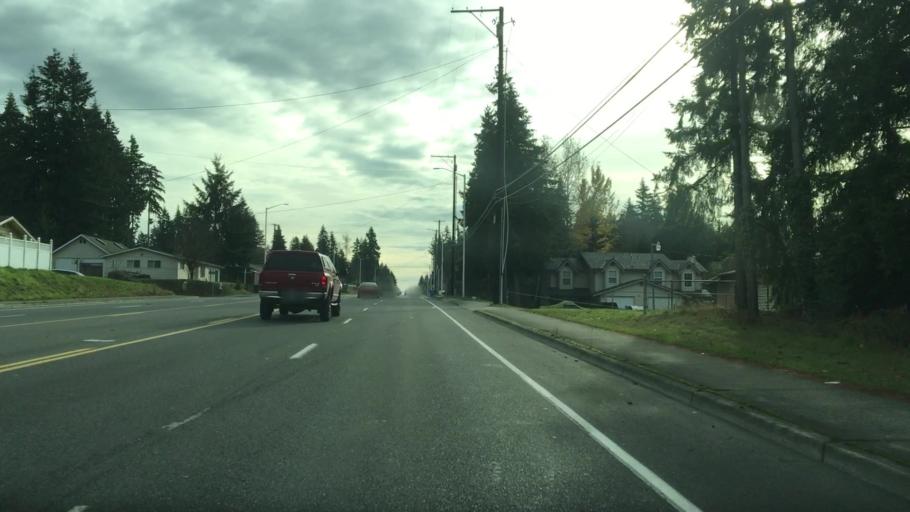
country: US
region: Washington
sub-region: Pierce County
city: South Hill
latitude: 47.1510
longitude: -122.3041
